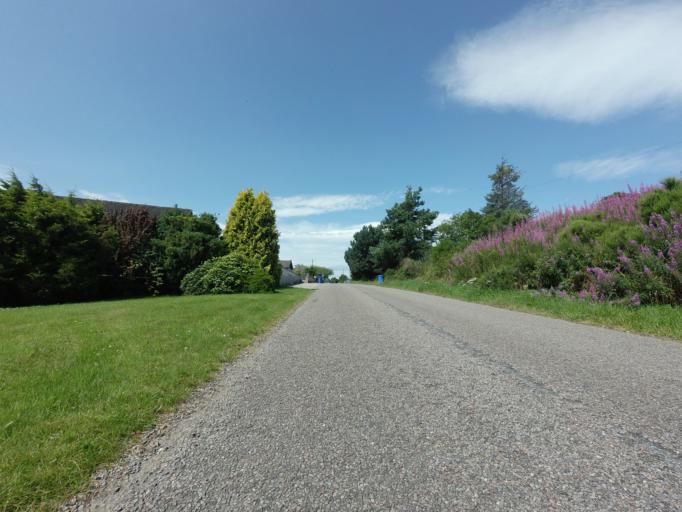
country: GB
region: Scotland
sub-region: Highland
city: Inverness
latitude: 57.5110
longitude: -4.2811
